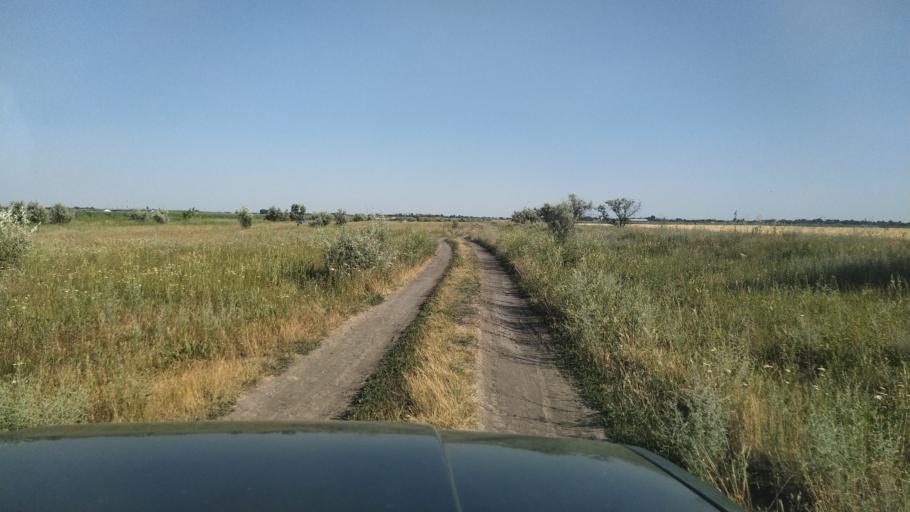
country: RU
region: Rostov
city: Kuleshovka
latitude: 47.1294
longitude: 39.6443
